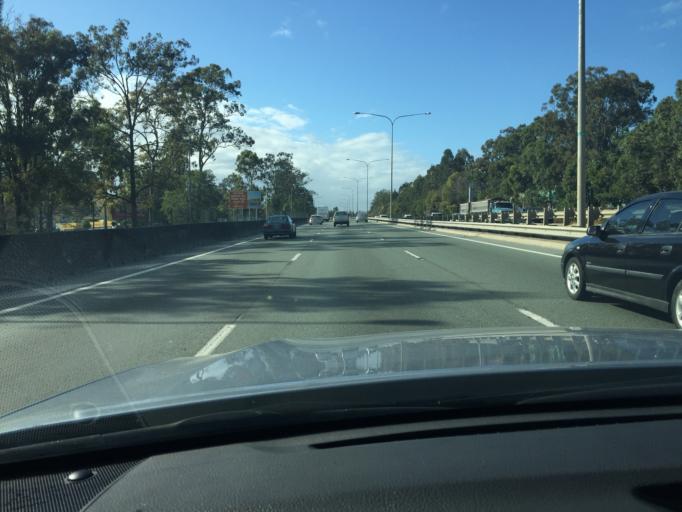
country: AU
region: Queensland
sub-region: Logan
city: Slacks Creek
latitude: -27.6701
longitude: 153.1787
